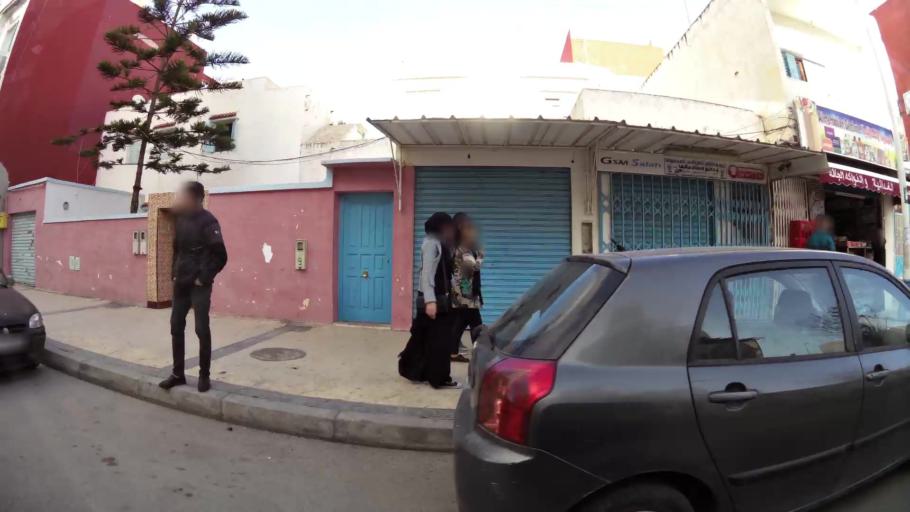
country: MA
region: Tanger-Tetouan
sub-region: Tetouan
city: Martil
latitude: 35.6182
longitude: -5.2769
